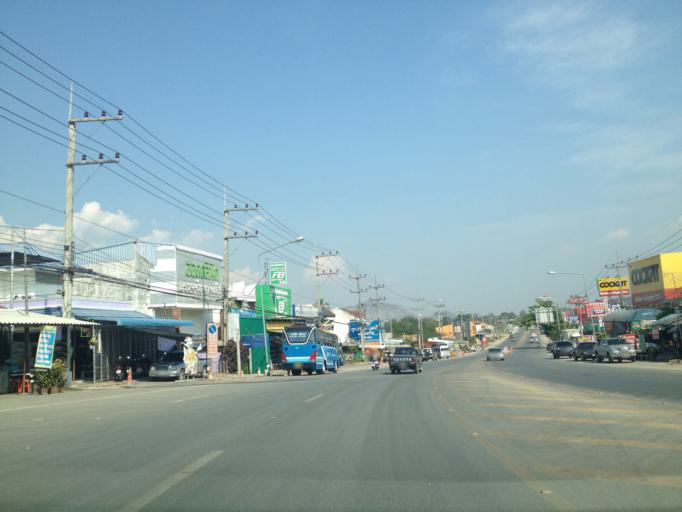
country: TH
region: Chiang Mai
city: Hot
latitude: 18.1964
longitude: 98.6113
